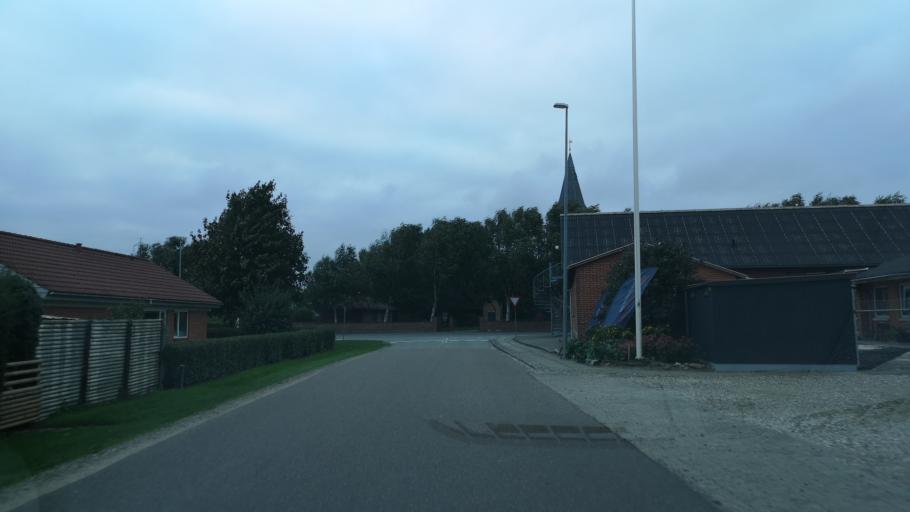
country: DK
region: Central Jutland
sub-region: Ringkobing-Skjern Kommune
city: Videbaek
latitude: 56.0681
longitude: 8.6078
